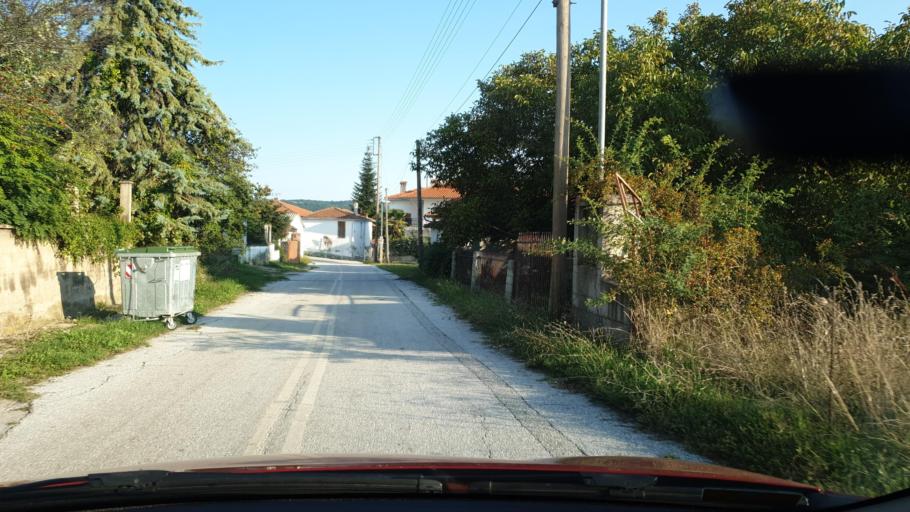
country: GR
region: Central Macedonia
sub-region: Nomos Chalkidikis
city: Galatista
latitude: 40.5171
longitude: 23.2825
